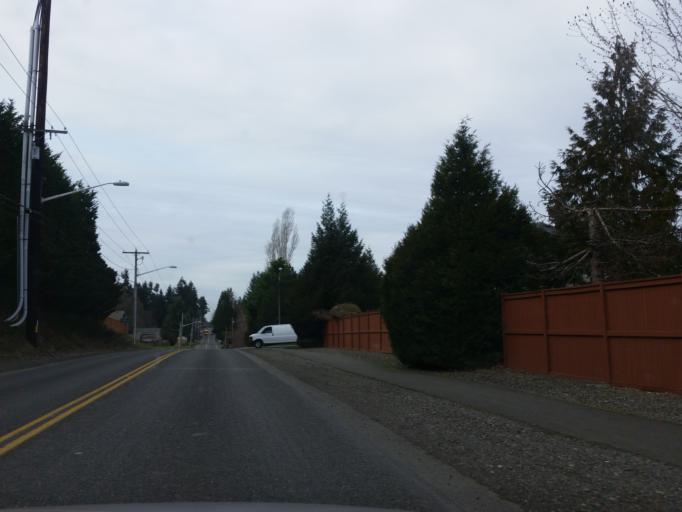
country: US
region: Washington
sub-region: Pierce County
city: South Hill
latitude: 47.1328
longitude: -122.2747
